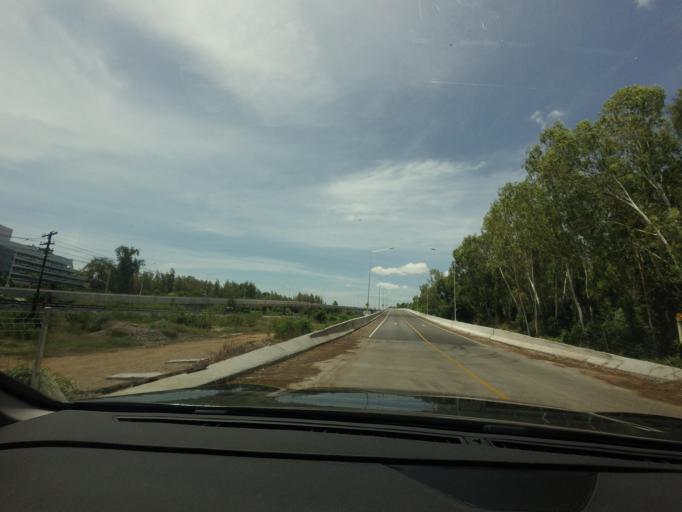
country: TH
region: Prachuap Khiri Khan
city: Hua Hin
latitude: 12.4953
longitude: 99.9722
